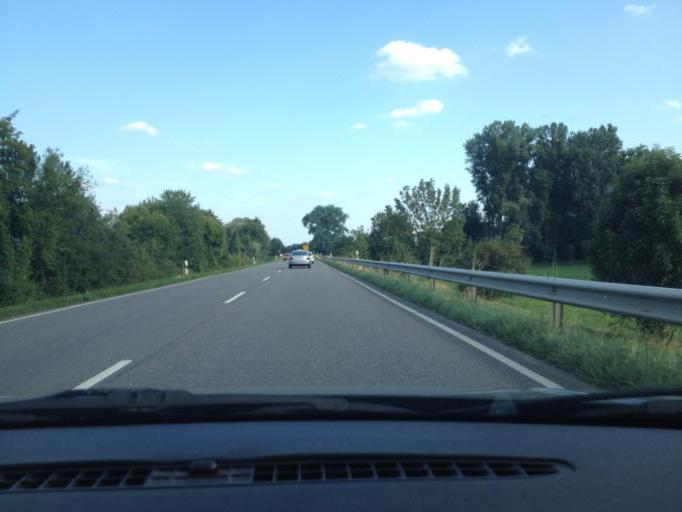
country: DE
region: Baden-Wuerttemberg
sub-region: Karlsruhe Region
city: Altlussheim
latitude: 49.3111
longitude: 8.4808
